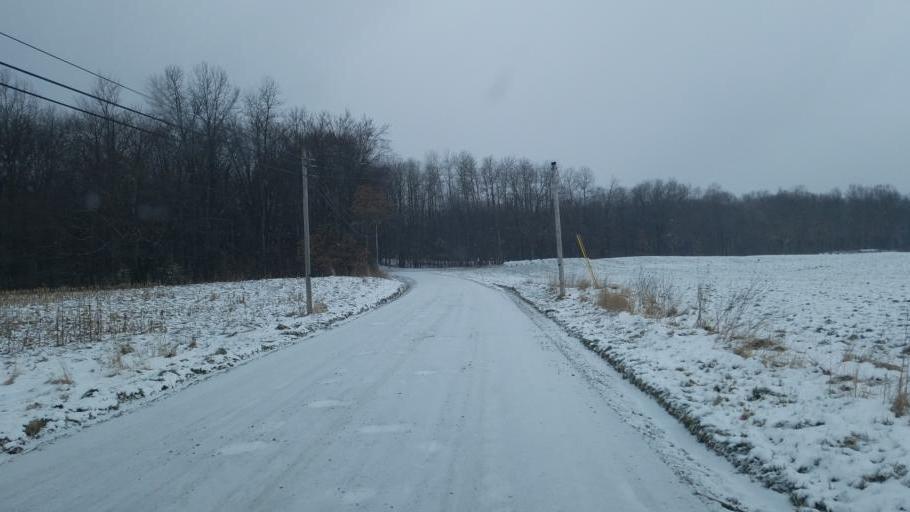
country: US
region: Pennsylvania
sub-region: Crawford County
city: Cochranton
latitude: 41.4622
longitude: -79.9704
